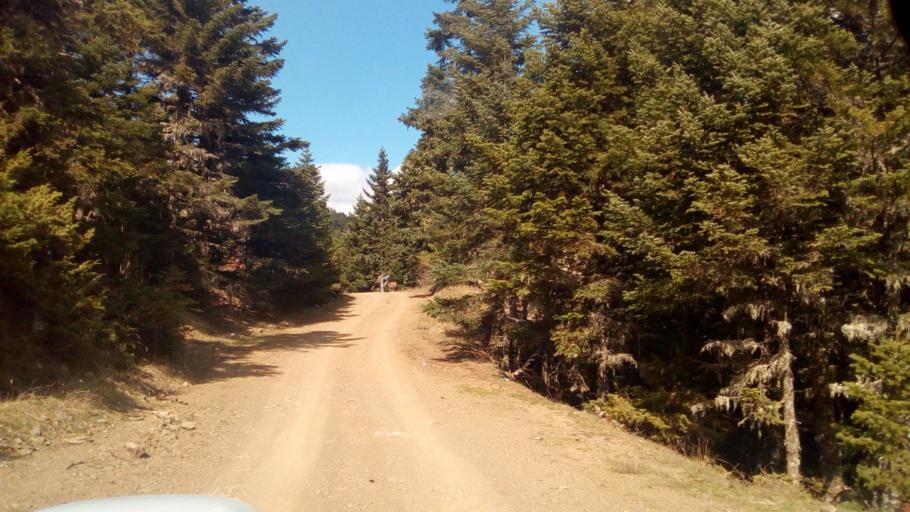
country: GR
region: West Greece
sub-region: Nomos Aitolias kai Akarnanias
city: Nafpaktos
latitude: 38.6394
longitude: 21.9419
